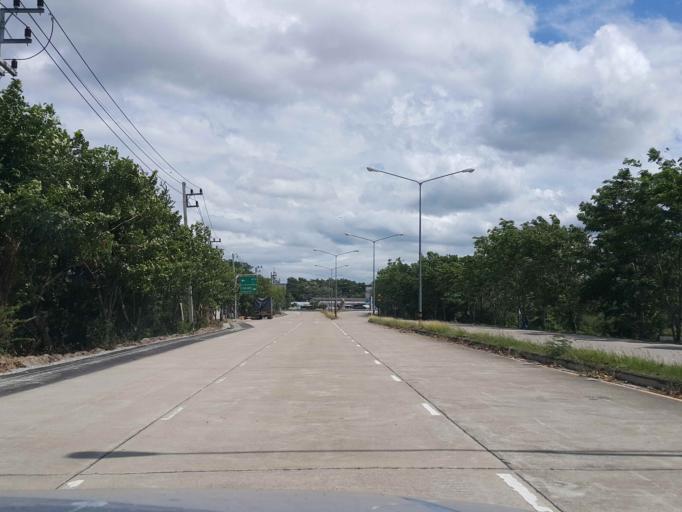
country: TH
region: Tak
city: Tak
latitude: 16.8561
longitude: 99.1166
